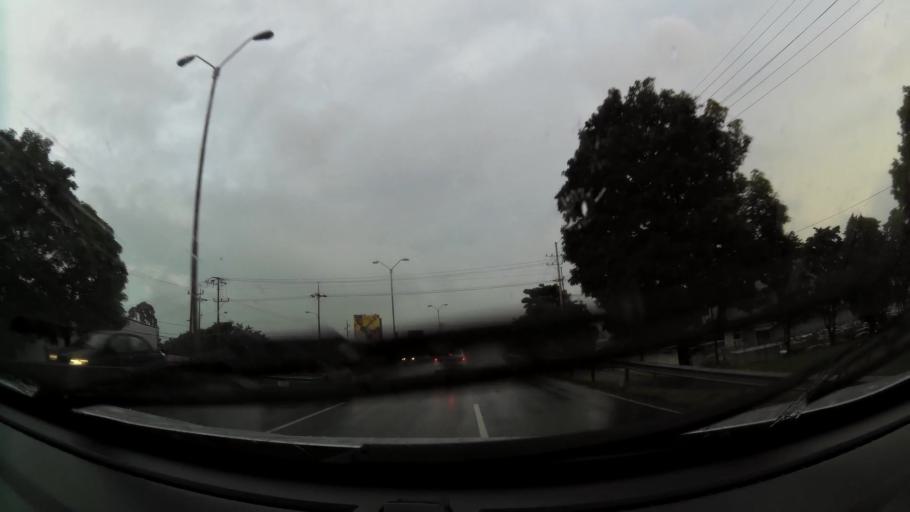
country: CR
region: Heredia
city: Llorente
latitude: 9.9959
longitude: -84.1680
